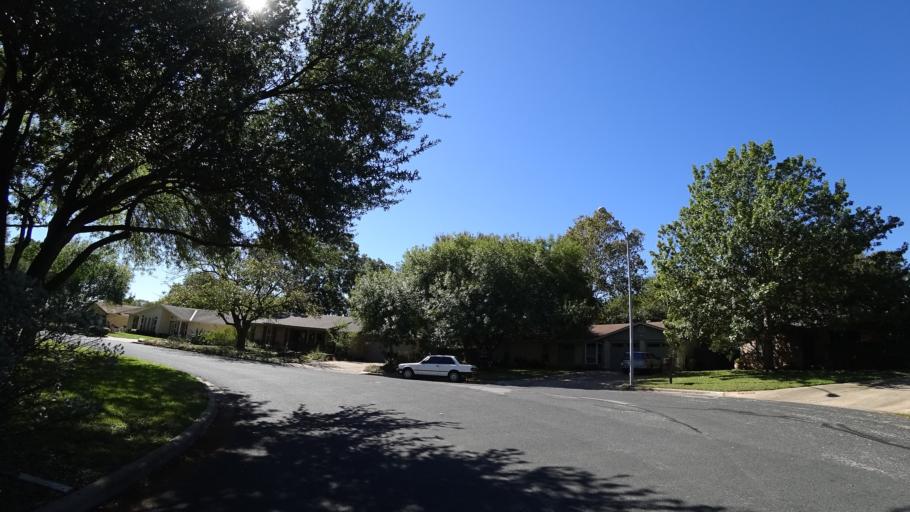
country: US
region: Texas
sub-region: Travis County
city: Rollingwood
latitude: 30.2189
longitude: -97.8002
